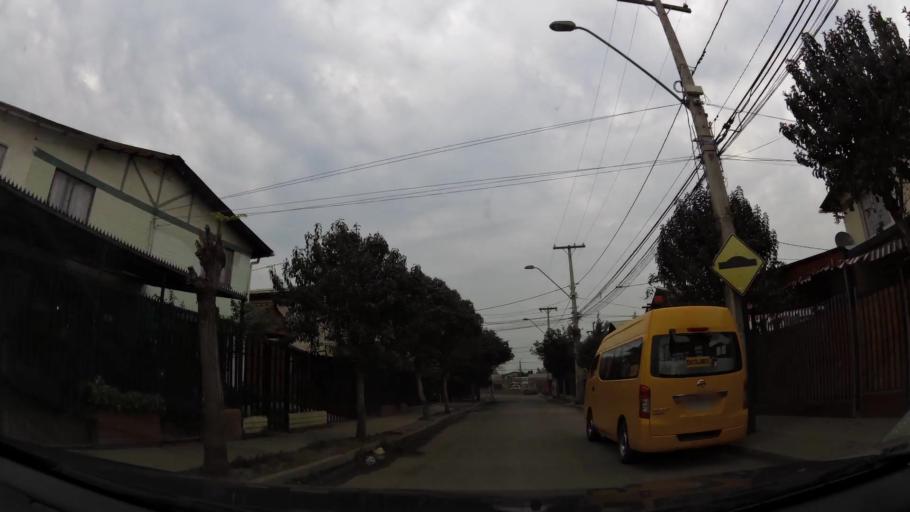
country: CL
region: Santiago Metropolitan
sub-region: Provincia de Chacabuco
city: Chicureo Abajo
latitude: -33.1912
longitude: -70.6758
